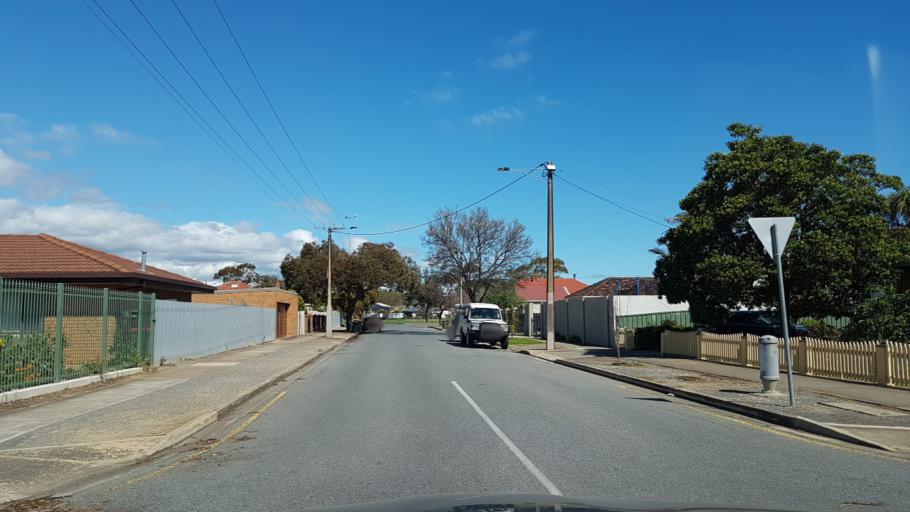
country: AU
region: South Australia
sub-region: Marion
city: Plympton Park
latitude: -34.9891
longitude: 138.5535
